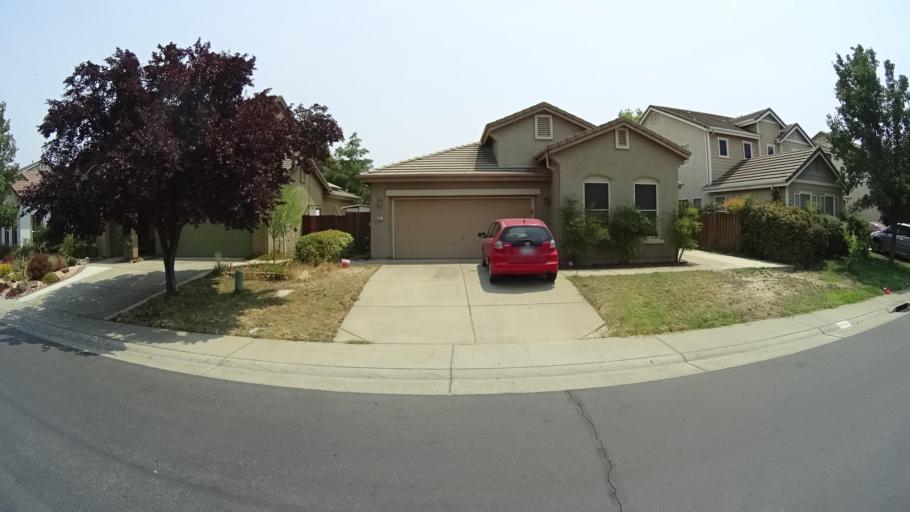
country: US
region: California
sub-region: Placer County
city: Roseville
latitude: 38.7980
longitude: -121.2821
